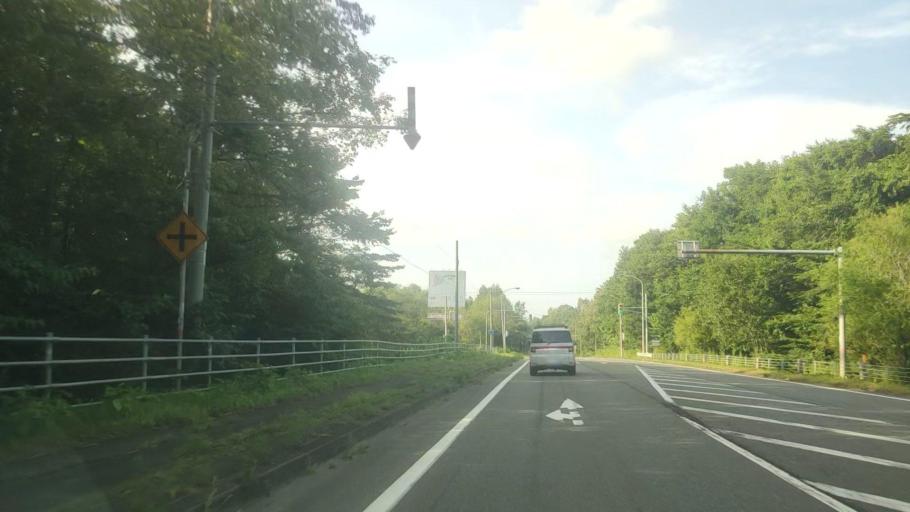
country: JP
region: Hokkaido
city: Chitose
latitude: 42.8657
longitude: 141.8226
